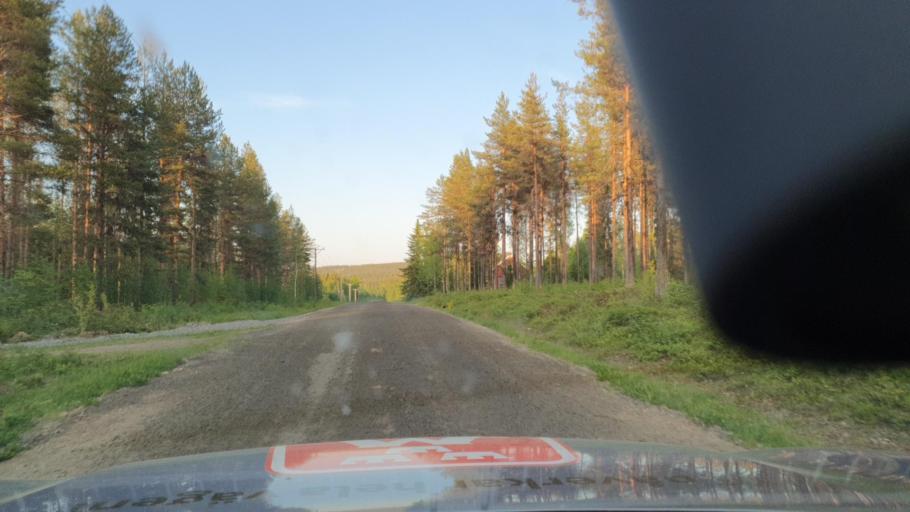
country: SE
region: Norrbotten
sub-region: Bodens Kommun
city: Boden
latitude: 66.0769
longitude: 21.6845
